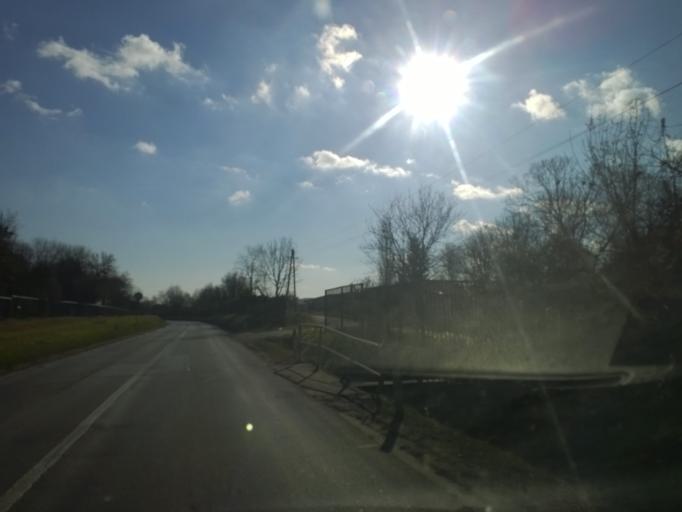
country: RS
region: Central Serbia
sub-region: Podunavski Okrug
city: Smederevo
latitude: 44.5998
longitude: 20.9641
